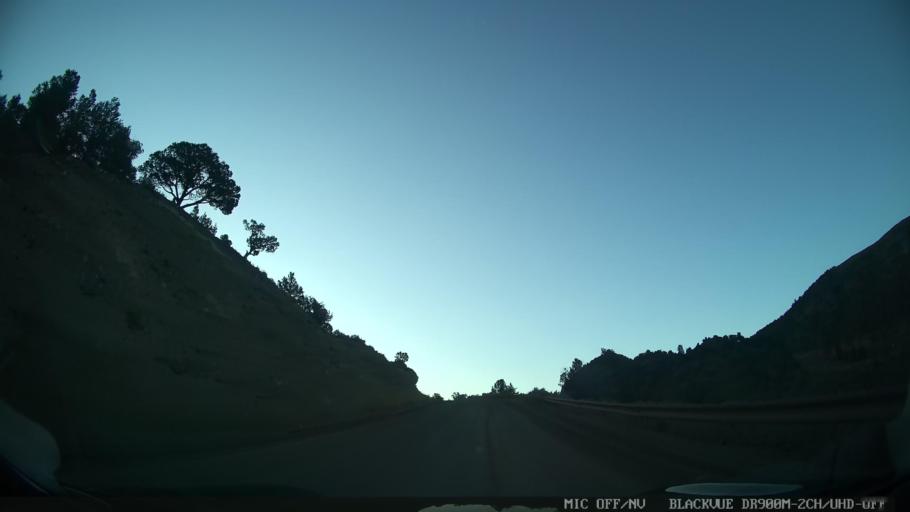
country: US
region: Colorado
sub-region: Eagle County
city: Edwards
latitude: 39.8579
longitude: -106.6459
